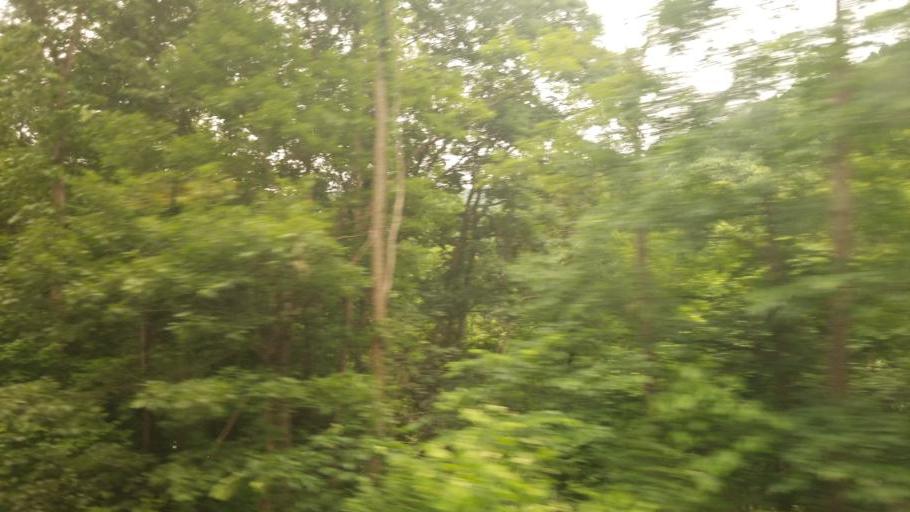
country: US
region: Pennsylvania
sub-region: Fayette County
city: South Connellsville
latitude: 39.9204
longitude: -79.4732
